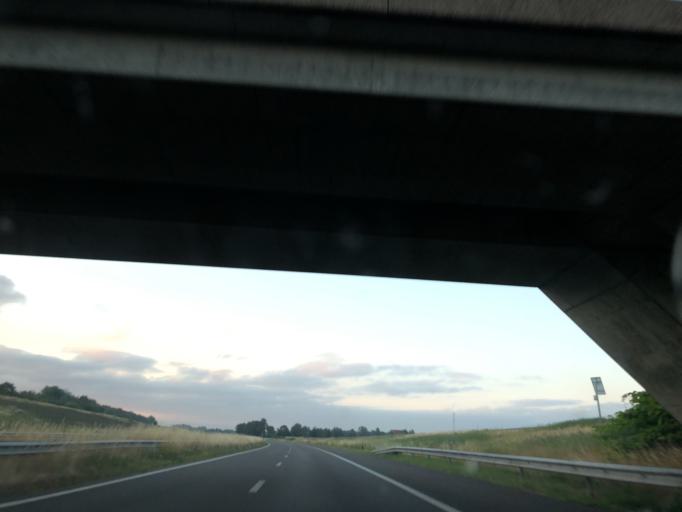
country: NL
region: Groningen
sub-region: Gemeente  Oldambt
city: Winschoten
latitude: 53.1695
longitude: 7.0007
